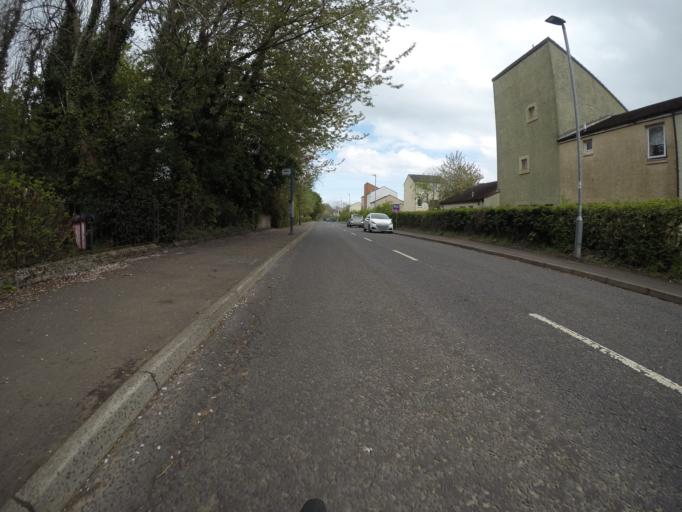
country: GB
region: Scotland
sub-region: North Ayrshire
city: Irvine
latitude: 55.6286
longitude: -4.6302
